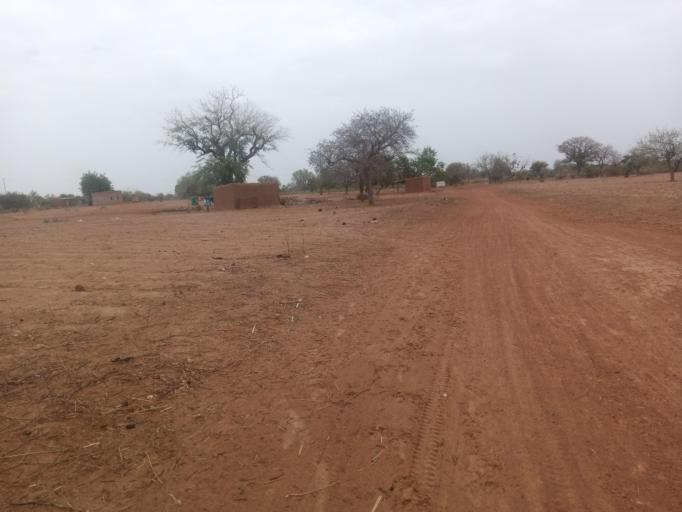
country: BF
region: Boucle du Mouhoun
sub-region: Province de la Kossi
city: Nouna
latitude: 12.8549
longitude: -4.0724
